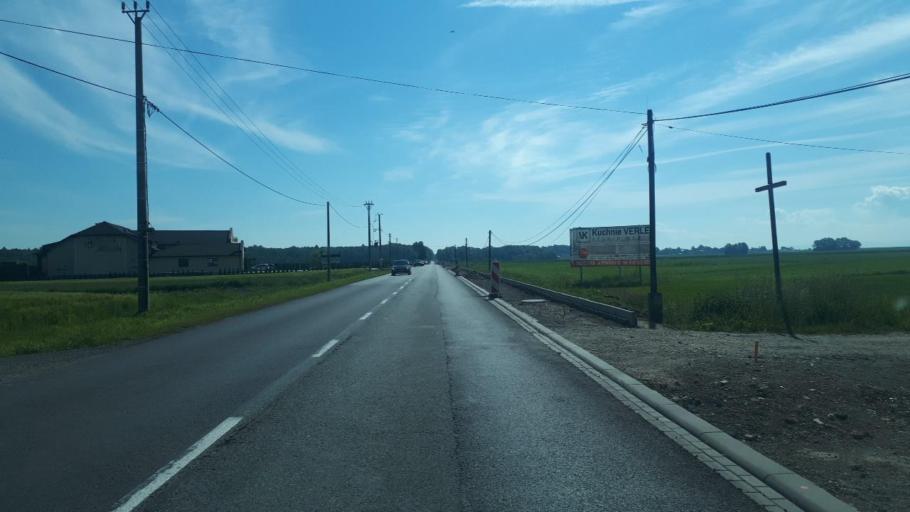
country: PL
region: Silesian Voivodeship
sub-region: Powiat pszczynski
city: Jankowice
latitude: 49.9711
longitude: 18.9989
